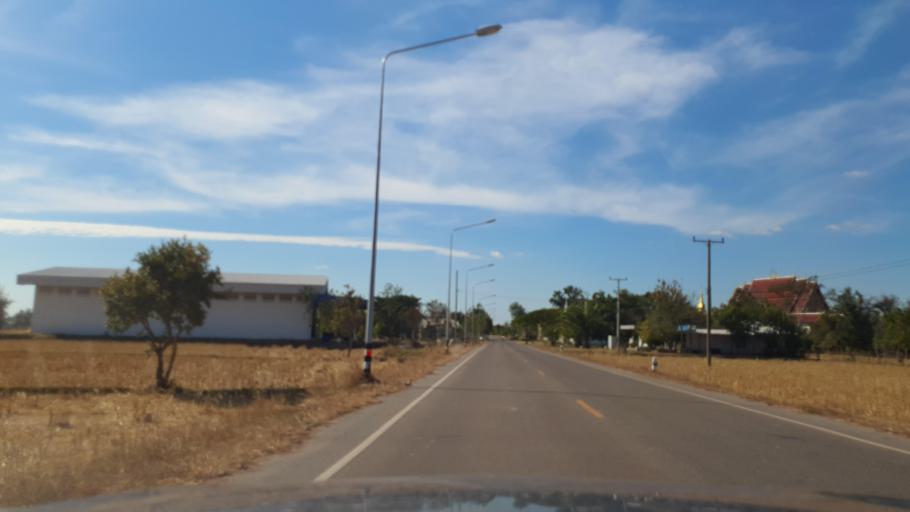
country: TH
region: Kalasin
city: Khao Wong
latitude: 16.6483
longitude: 104.1587
